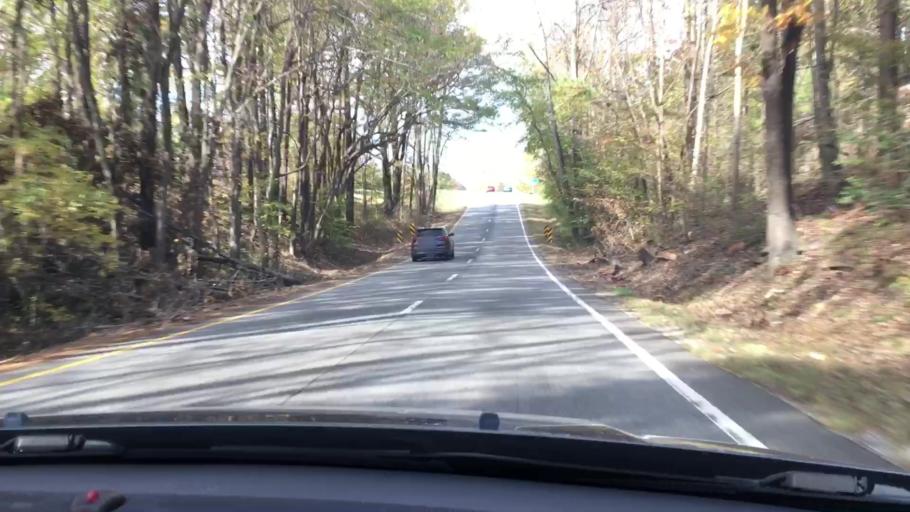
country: US
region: Virginia
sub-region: James City County
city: Williamsburg
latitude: 37.3263
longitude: -76.7392
